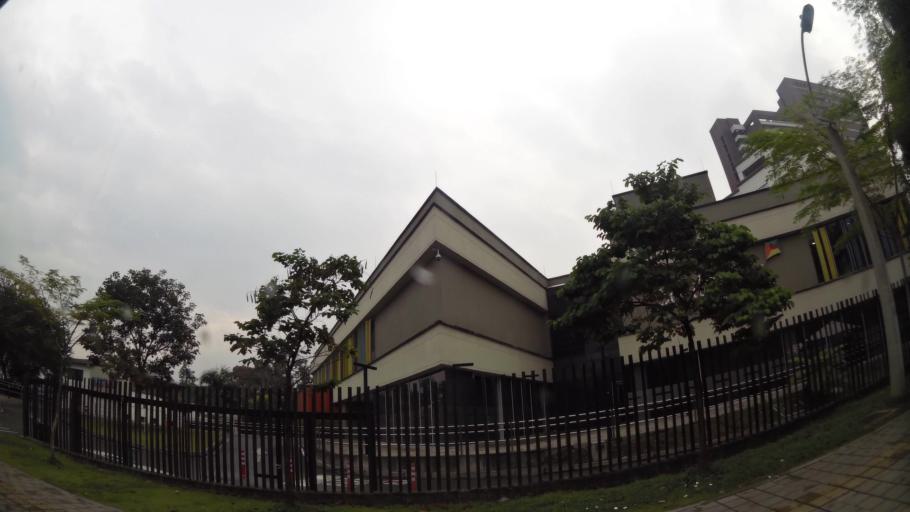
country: CO
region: Antioquia
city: Medellin
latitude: 6.2148
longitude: -75.5716
